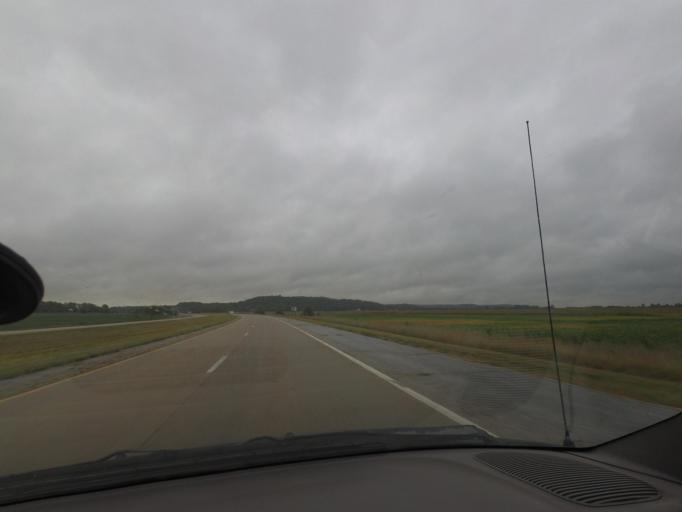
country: US
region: Illinois
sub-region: Adams County
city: Payson
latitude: 39.7178
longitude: -91.1864
